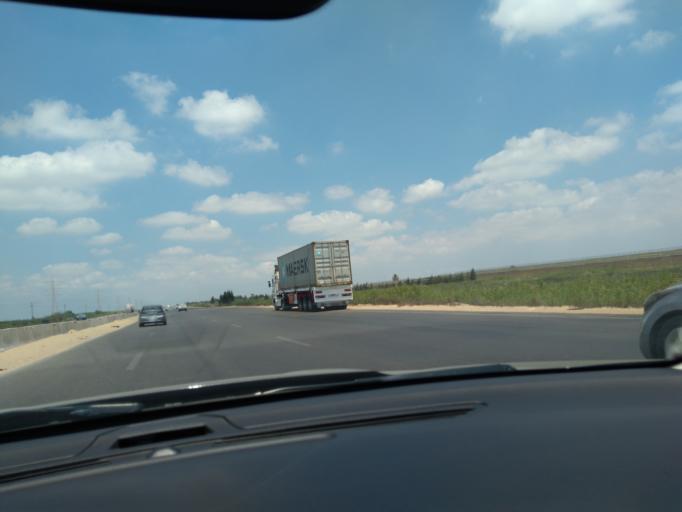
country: EG
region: Muhafazat Bur Sa`id
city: Port Said
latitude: 30.9856
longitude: 32.3078
